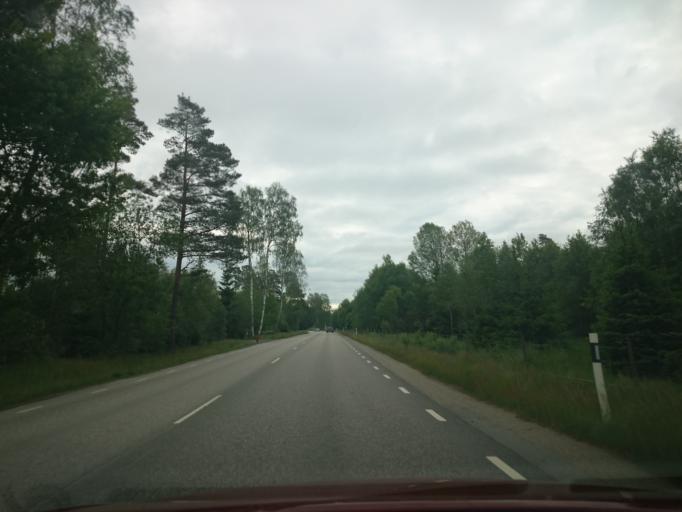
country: SE
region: Vaestra Goetaland
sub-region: Harryda Kommun
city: Hindas
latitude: 57.6970
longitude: 12.3556
